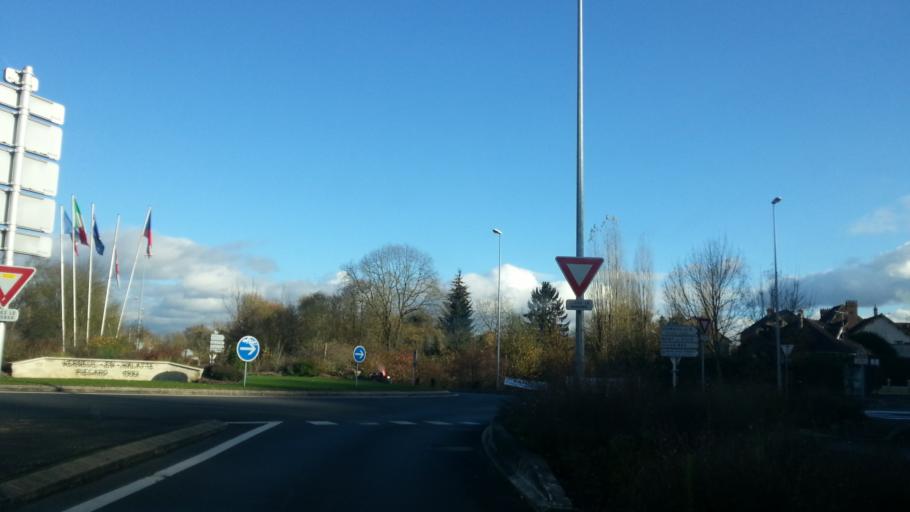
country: FR
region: Picardie
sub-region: Departement de l'Oise
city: Verneuil-en-Halatte
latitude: 49.2789
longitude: 2.5085
